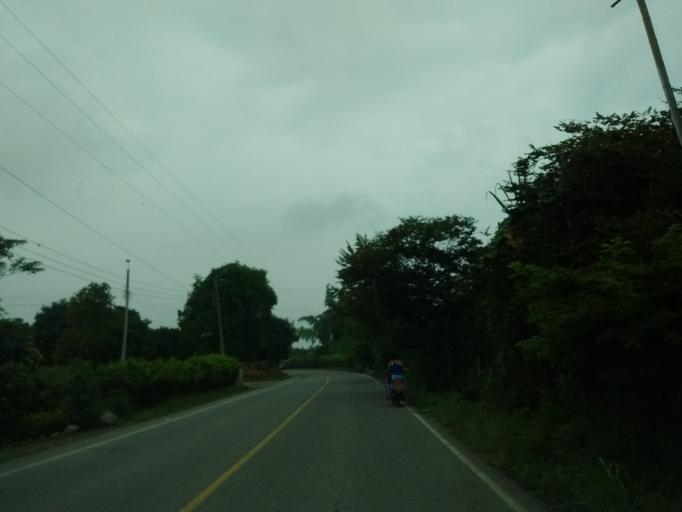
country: CO
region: Cauca
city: Padilla
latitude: 3.2298
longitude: -76.3233
